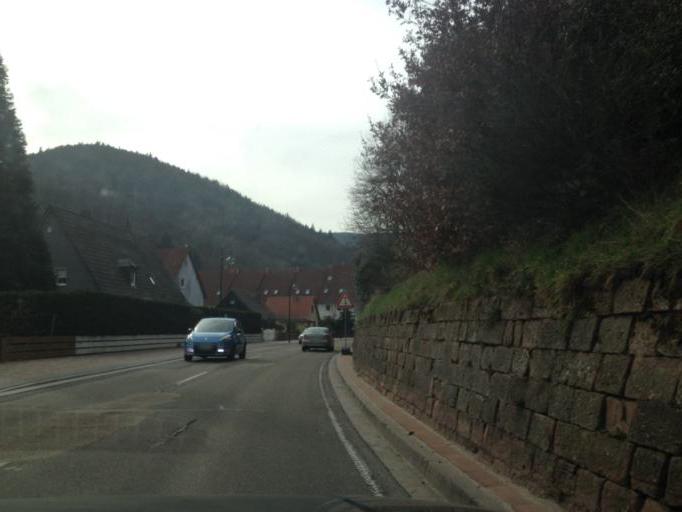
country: DE
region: Rheinland-Pfalz
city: Bad Duerkheim
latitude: 49.4605
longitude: 8.1361
